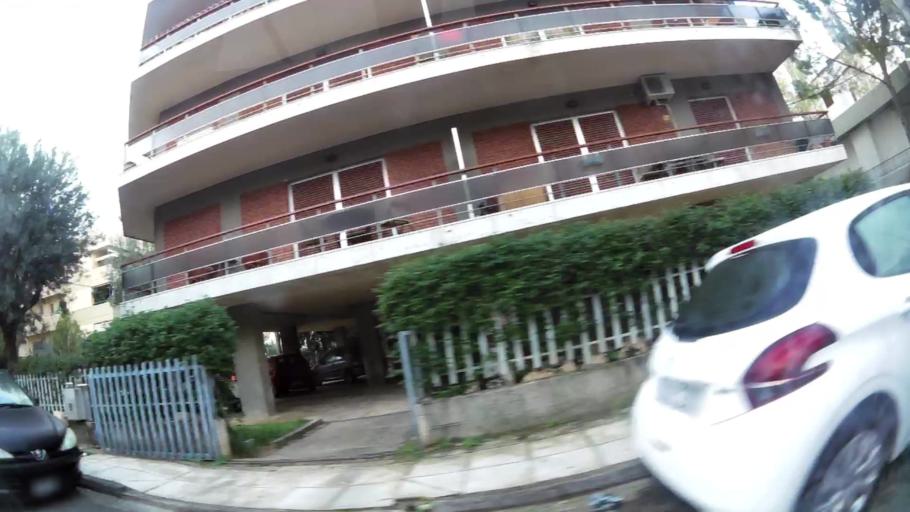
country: GR
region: Attica
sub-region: Nomarchia Athinas
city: Melissia
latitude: 38.0422
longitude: 23.8309
